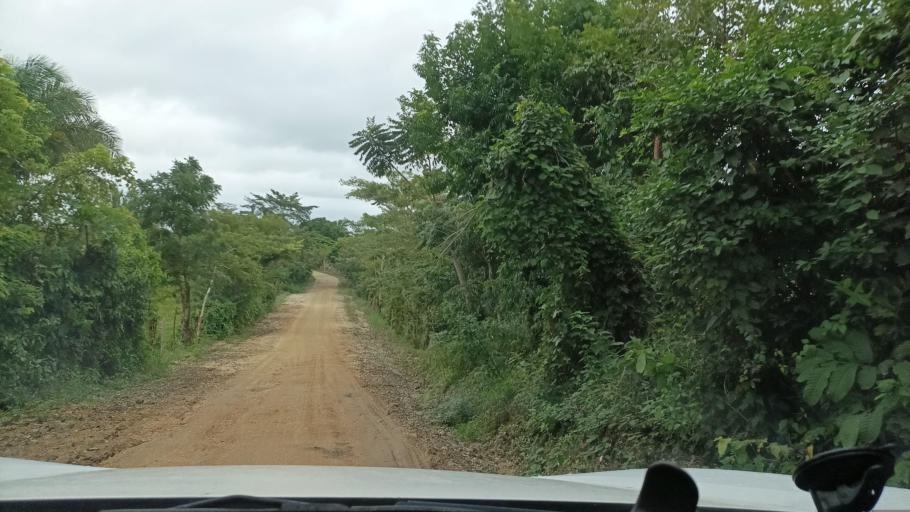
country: MX
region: Veracruz
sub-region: Moloacan
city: Cuichapa
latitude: 17.7883
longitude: -94.3587
